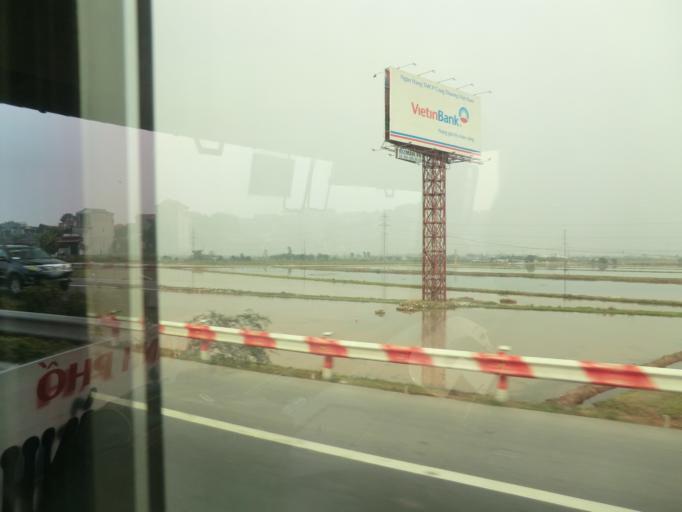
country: VN
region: Ha Noi
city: Thuong Tin
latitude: 20.8862
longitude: 105.8703
